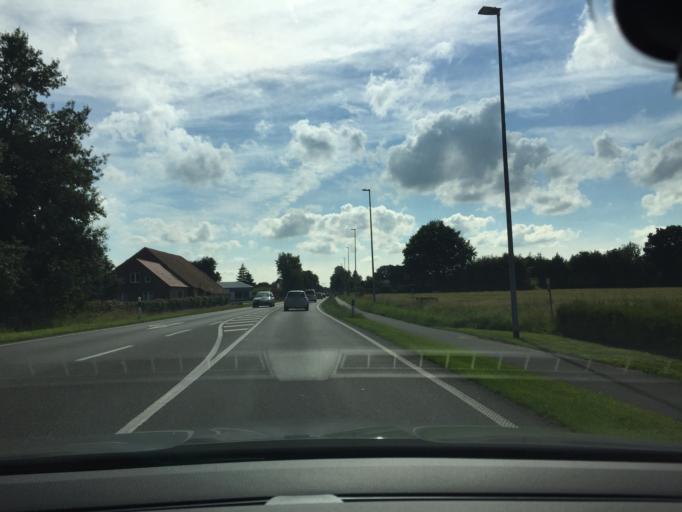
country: DE
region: Lower Saxony
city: Blomberg
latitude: 53.5145
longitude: 7.5587
